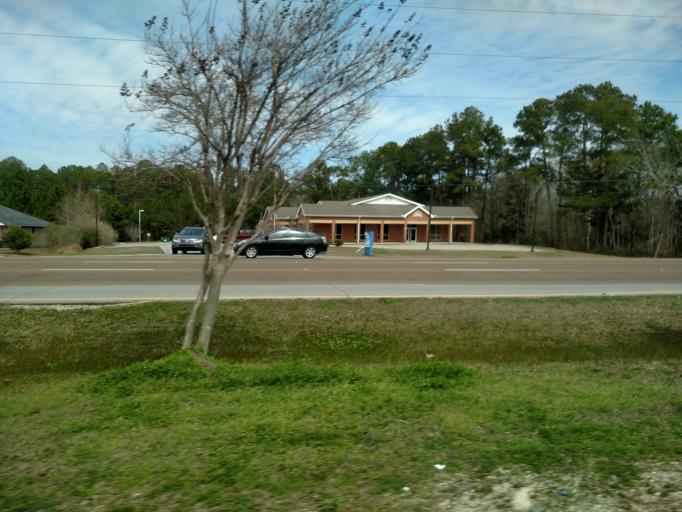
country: US
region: Mississippi
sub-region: Jackson County
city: Gautier
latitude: 30.3897
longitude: -88.6385
